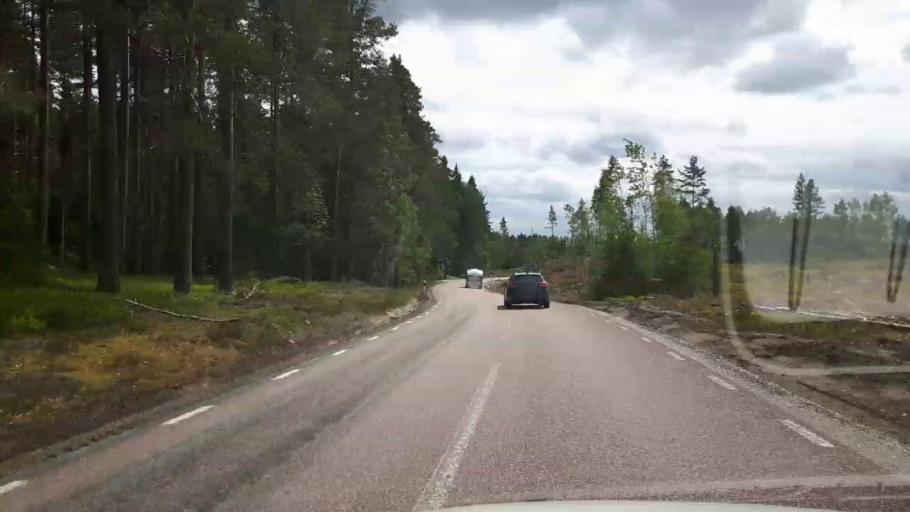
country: SE
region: Vaestmanland
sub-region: Skinnskattebergs Kommun
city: Skinnskatteberg
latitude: 59.8065
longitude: 15.8418
